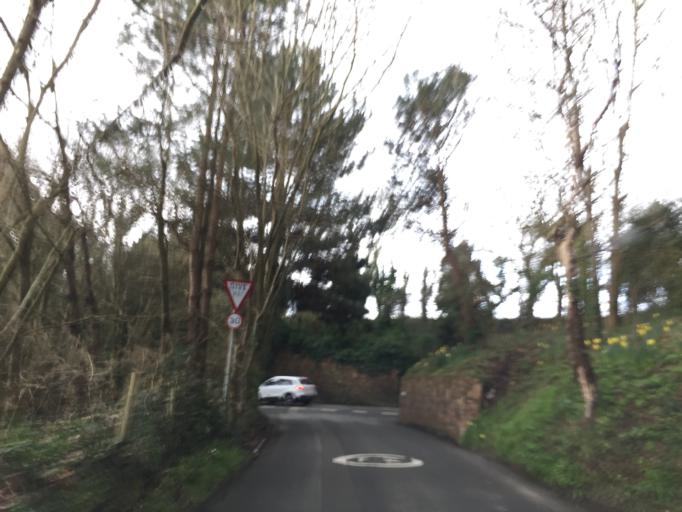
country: JE
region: St Helier
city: Saint Helier
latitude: 49.2015
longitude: -2.1374
